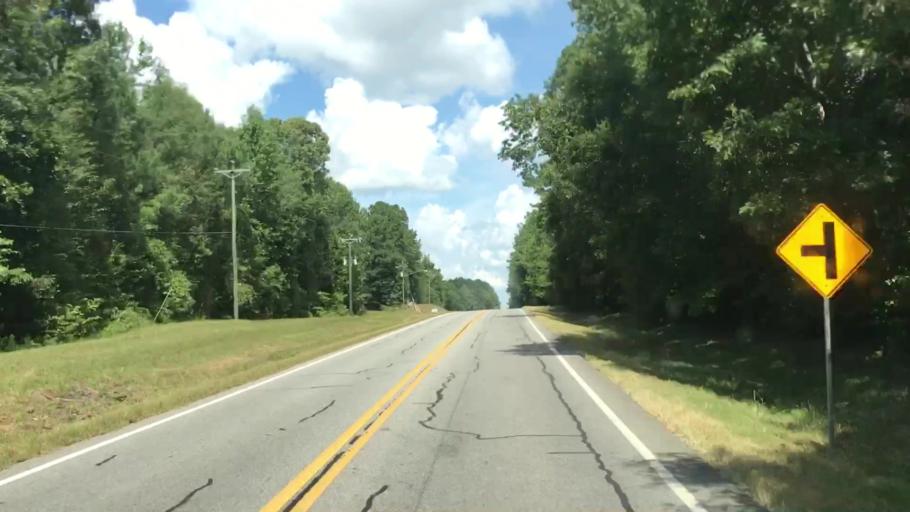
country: US
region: Georgia
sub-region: Oconee County
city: Watkinsville
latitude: 33.7641
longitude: -83.3093
